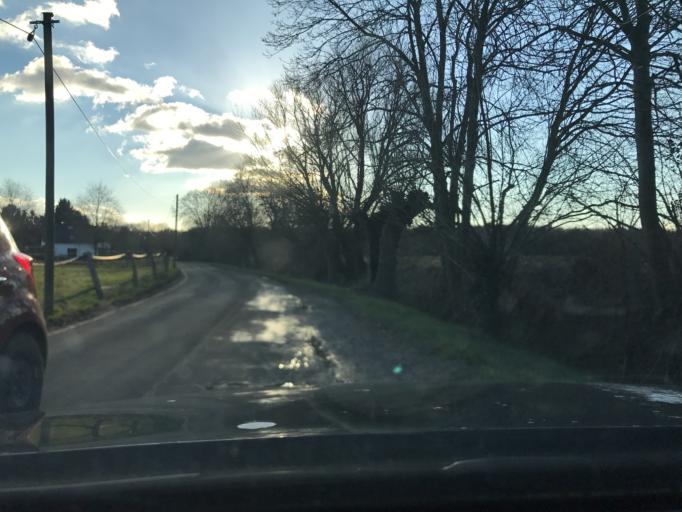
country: DE
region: North Rhine-Westphalia
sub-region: Regierungsbezirk Dusseldorf
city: Krefeld
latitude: 51.3637
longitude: 6.6054
